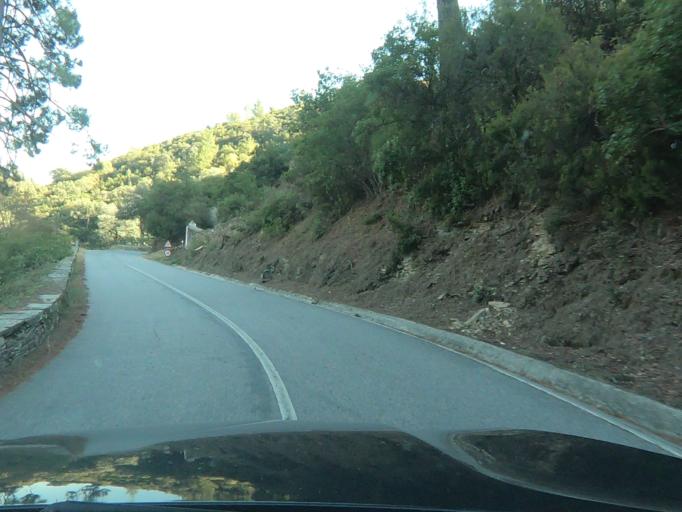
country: PT
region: Vila Real
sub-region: Sabrosa
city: Vilela
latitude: 41.2012
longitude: -7.5623
